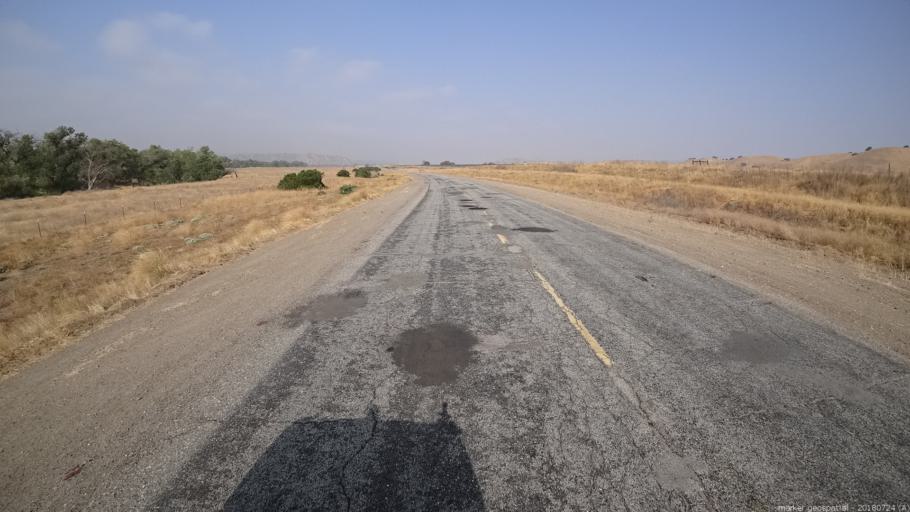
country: US
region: California
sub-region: San Luis Obispo County
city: San Miguel
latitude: 35.8619
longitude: -120.7711
